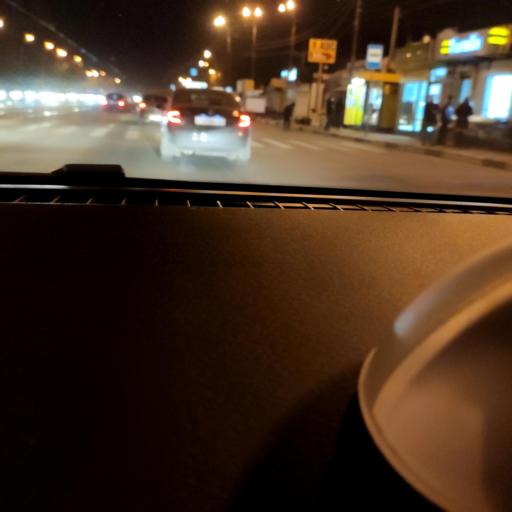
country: RU
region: Samara
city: Smyshlyayevka
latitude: 53.2098
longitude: 50.2743
